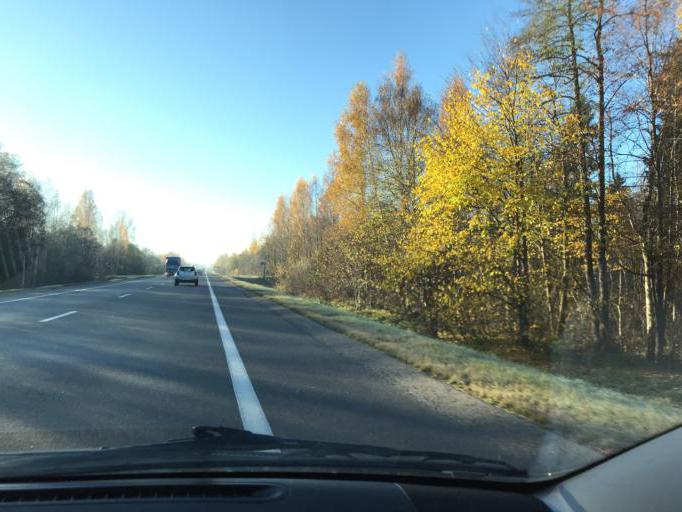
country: BY
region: Vitebsk
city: Vitebsk
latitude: 54.9790
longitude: 30.3472
